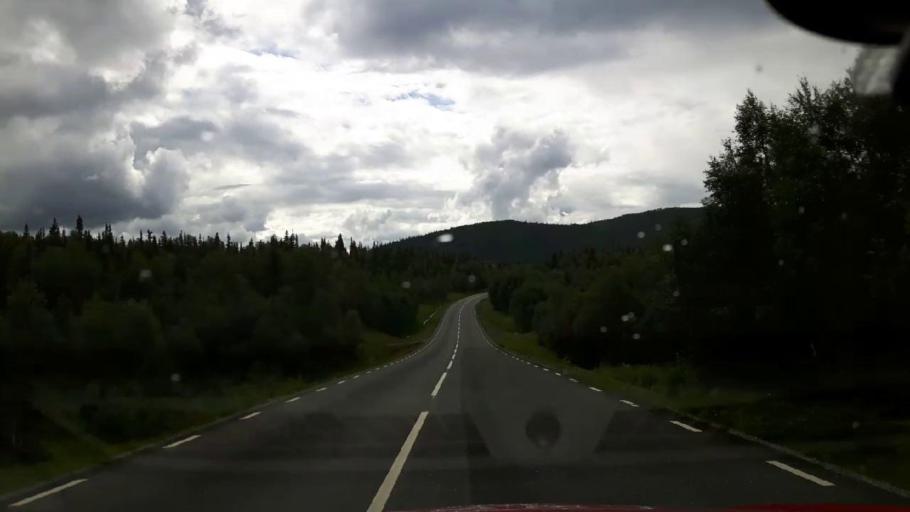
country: NO
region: Nord-Trondelag
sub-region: Royrvik
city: Royrvik
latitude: 64.8962
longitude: 14.1915
